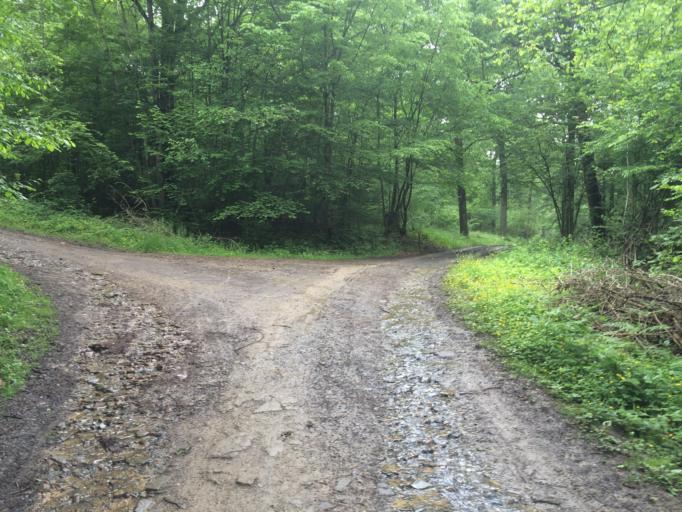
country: BE
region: Wallonia
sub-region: Province de Namur
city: Yvoir
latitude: 50.3272
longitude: 4.9502
